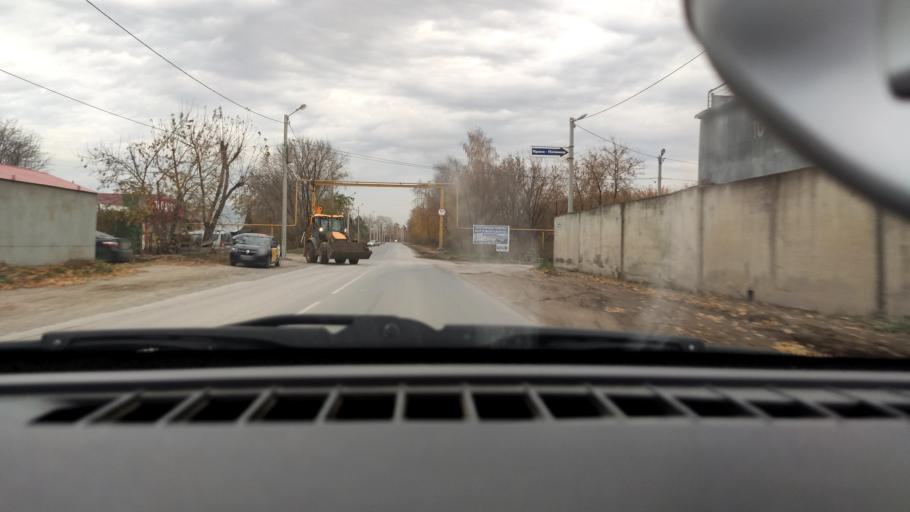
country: RU
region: Perm
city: Kondratovo
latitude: 57.9496
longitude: 56.1396
